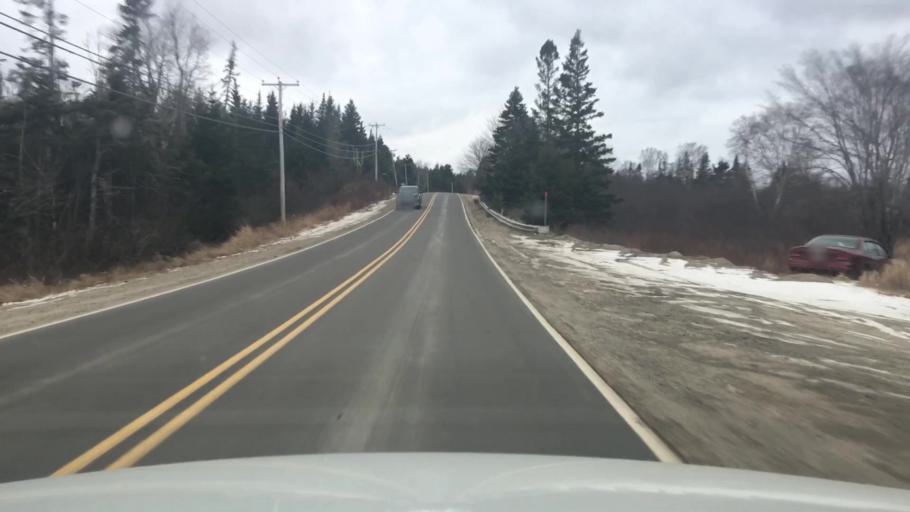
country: US
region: Maine
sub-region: Washington County
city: Jonesport
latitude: 44.5590
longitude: -67.6298
